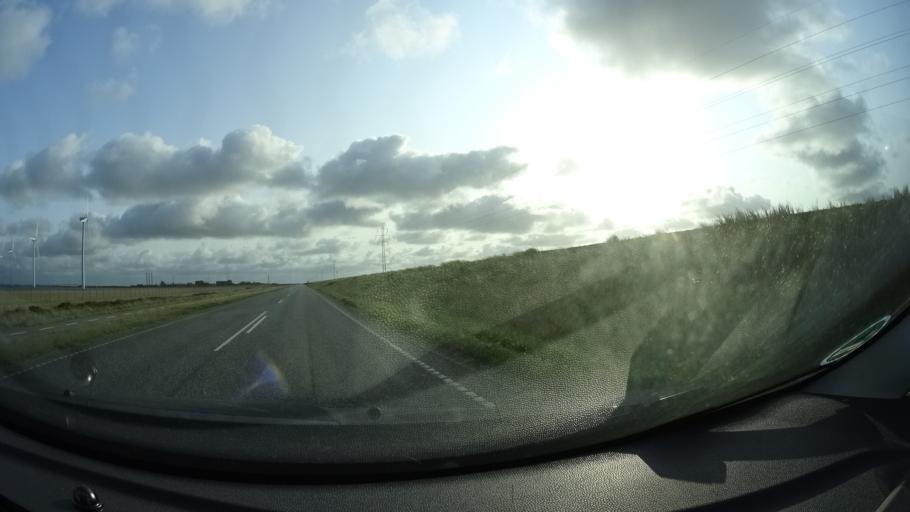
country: DK
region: Central Jutland
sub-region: Lemvig Kommune
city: Thyboron
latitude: 56.6752
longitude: 8.2177
